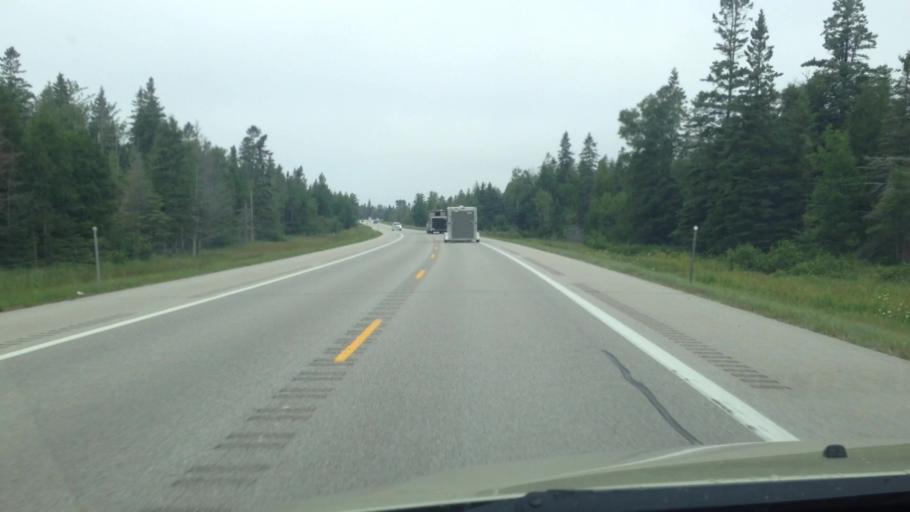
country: US
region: Michigan
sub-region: Luce County
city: Newberry
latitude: 46.0731
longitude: -85.2787
